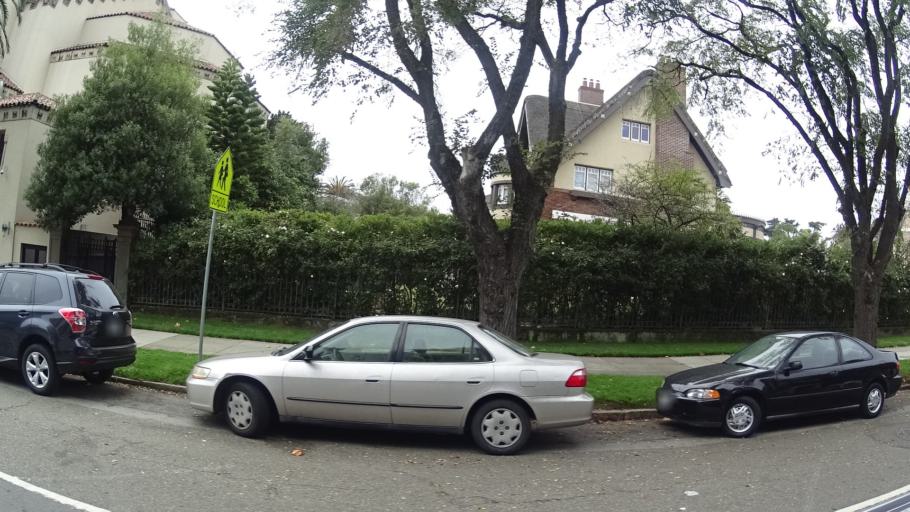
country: US
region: California
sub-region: San Francisco County
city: San Francisco
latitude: 37.7880
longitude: -122.4594
